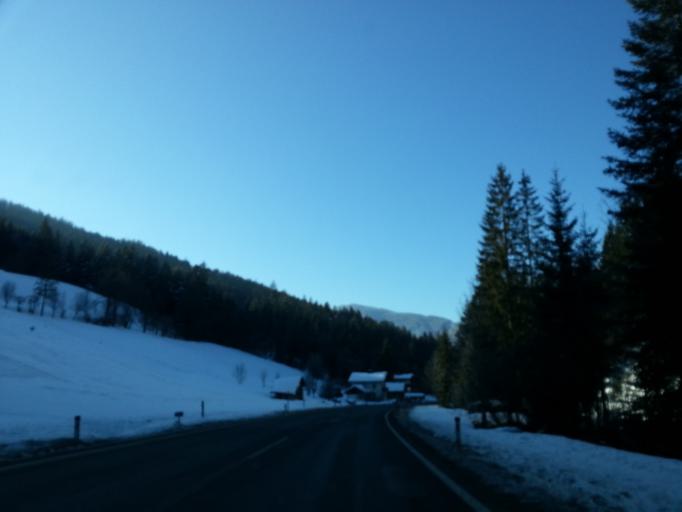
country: AT
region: Salzburg
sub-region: Politischer Bezirk Sankt Johann im Pongau
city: Eben im Pongau
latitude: 47.4413
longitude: 13.3625
